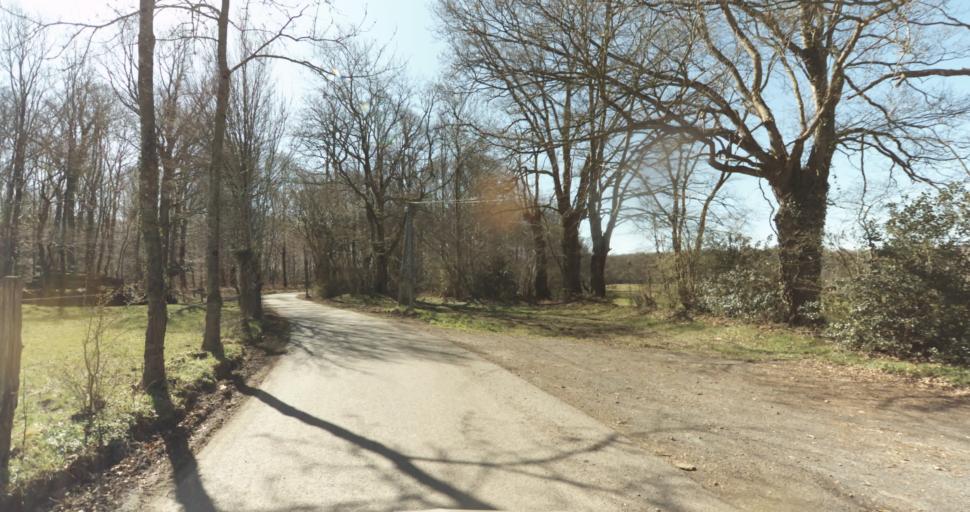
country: FR
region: Lower Normandy
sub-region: Departement du Calvados
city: Livarot
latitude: 48.9740
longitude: 0.0950
